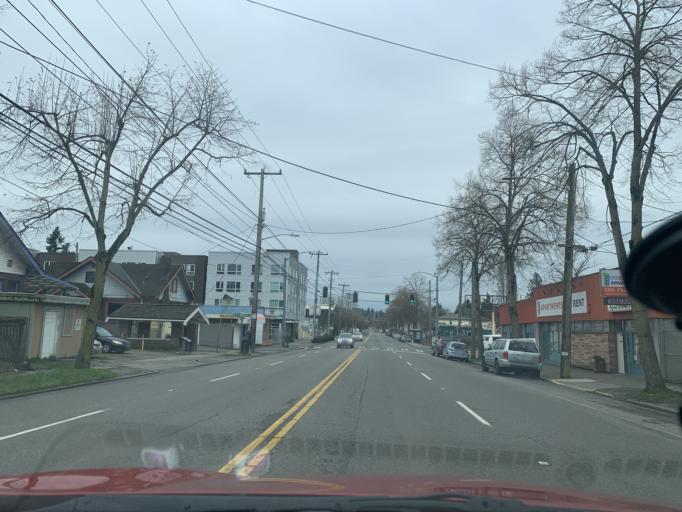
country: US
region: Washington
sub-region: King County
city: Bryn Mawr-Skyway
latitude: 47.5344
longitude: -122.2700
